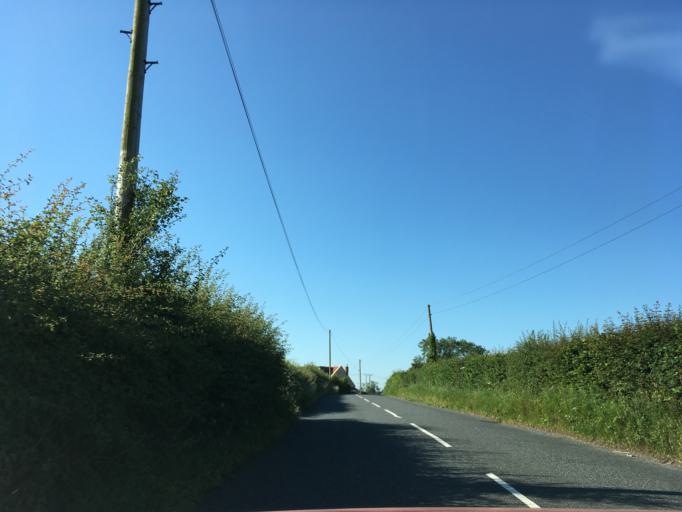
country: GB
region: England
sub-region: South Gloucestershire
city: Pucklechurch
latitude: 51.4661
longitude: -2.4263
